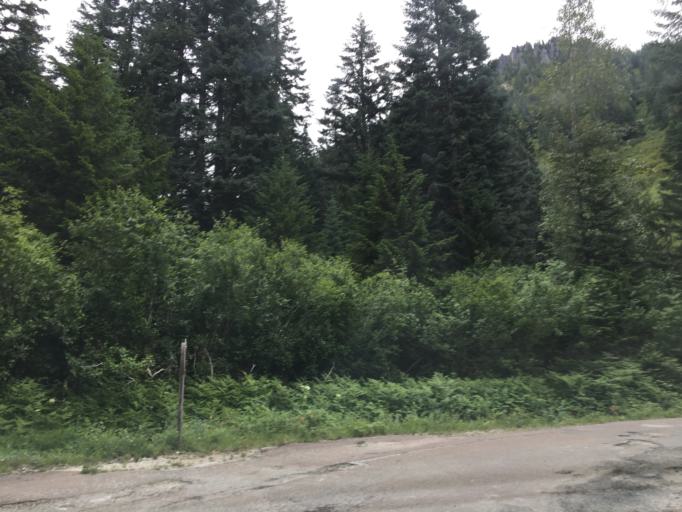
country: US
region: Washington
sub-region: Chelan County
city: Leavenworth
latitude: 47.7533
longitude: -121.1284
